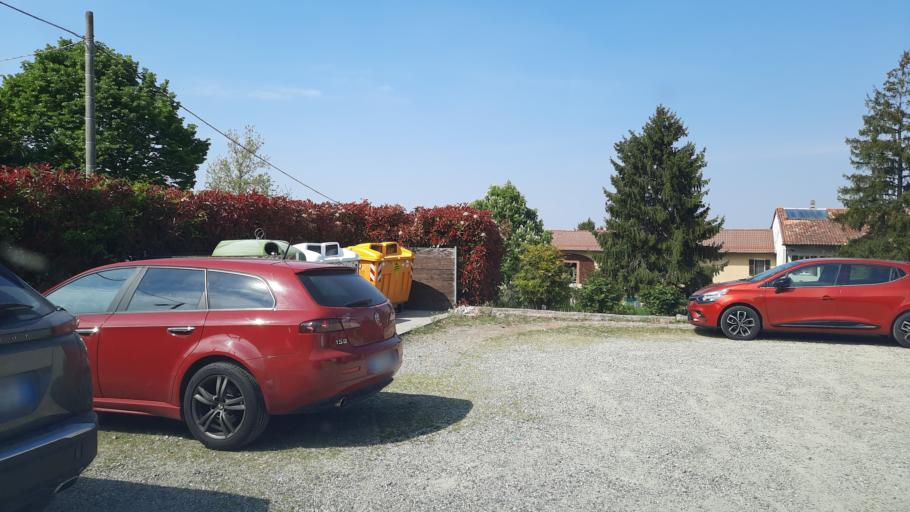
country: IT
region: Piedmont
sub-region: Provincia di Alessandria
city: Camino
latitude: 45.1724
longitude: 8.2652
